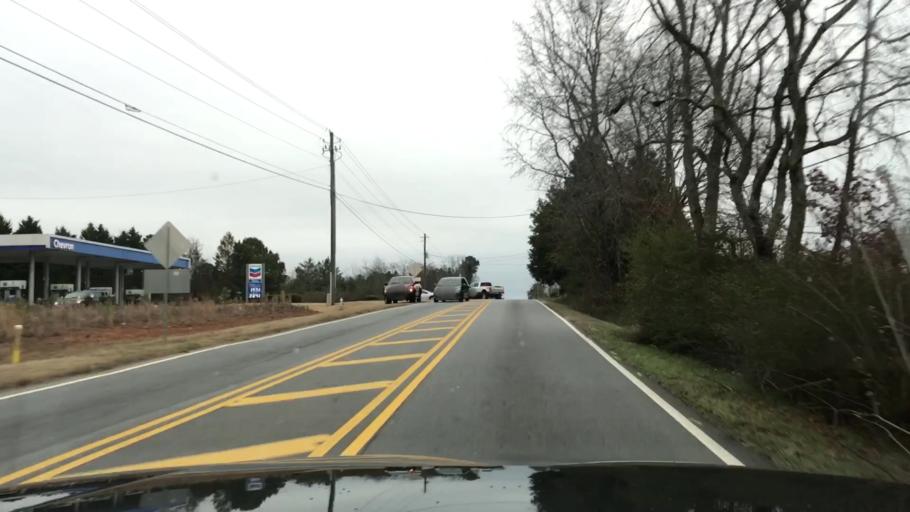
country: US
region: Georgia
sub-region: Gwinnett County
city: Dacula
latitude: 33.9716
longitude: -83.8900
